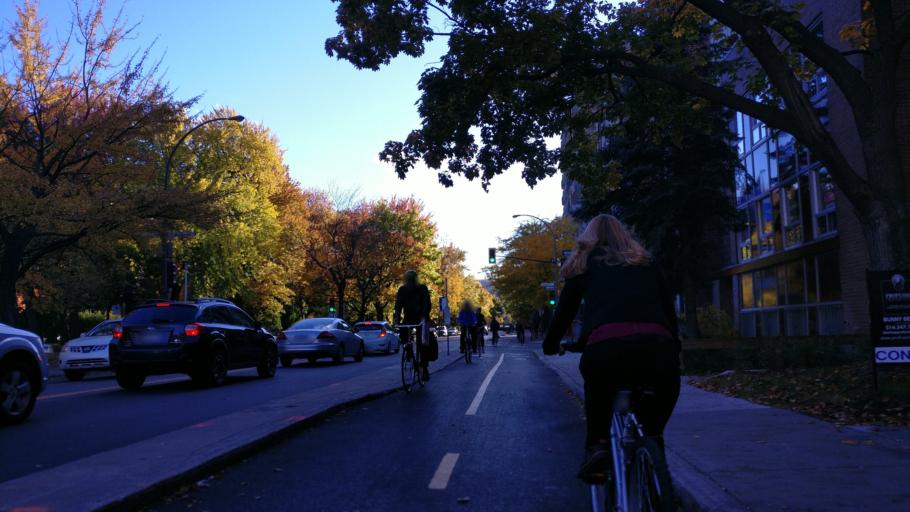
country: CA
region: Quebec
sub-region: Montreal
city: Montreal
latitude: 45.5302
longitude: -73.5699
